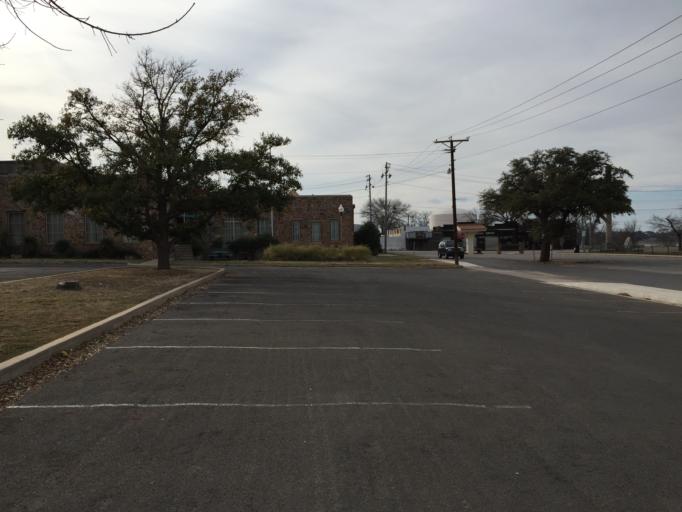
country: US
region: Texas
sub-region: Llano County
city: Llano
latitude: 30.7513
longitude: -98.6749
